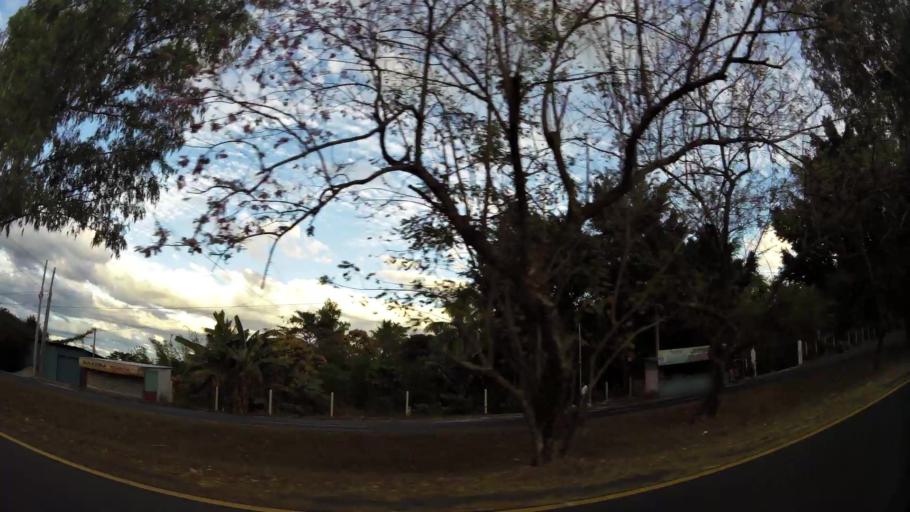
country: SV
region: San Vicente
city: San Sebastian
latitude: 13.6859
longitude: -88.8493
